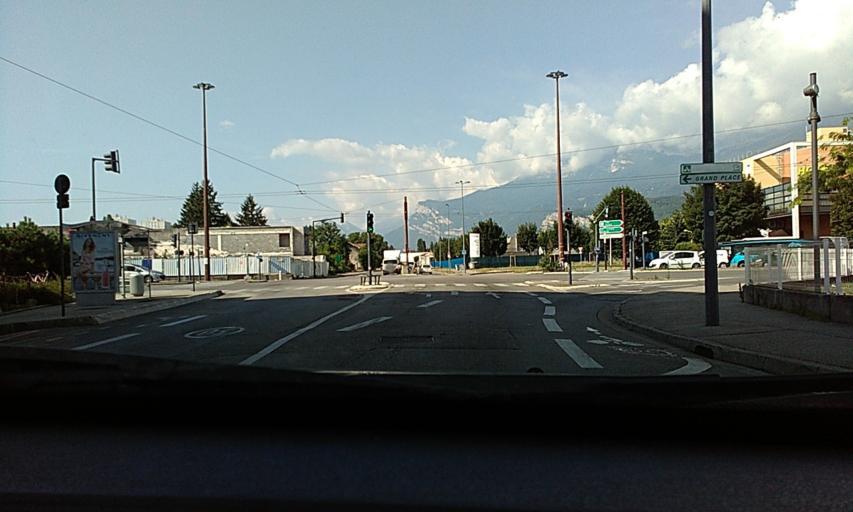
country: FR
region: Rhone-Alpes
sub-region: Departement de l'Isere
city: Grenoble
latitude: 45.1623
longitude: 5.7161
